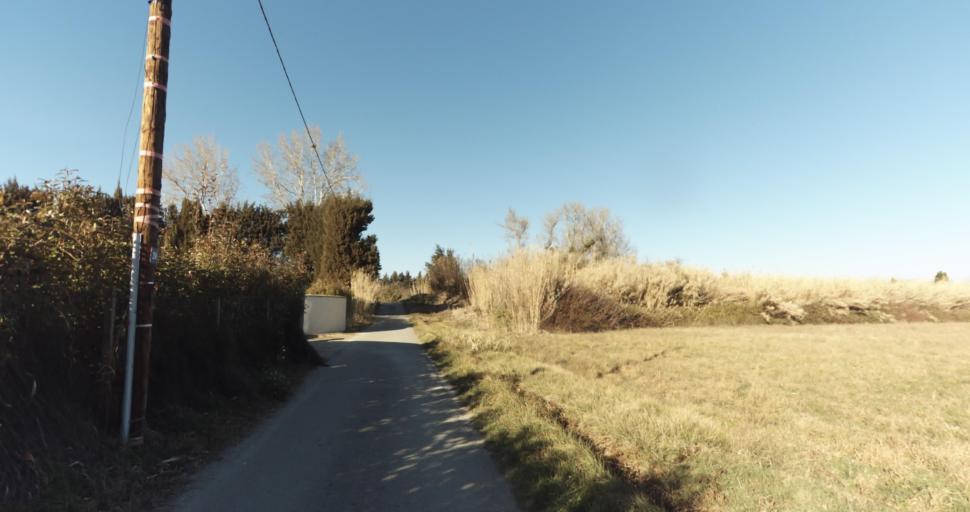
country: FR
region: Provence-Alpes-Cote d'Azur
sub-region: Departement des Bouches-du-Rhone
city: Barbentane
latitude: 43.9138
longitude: 4.7708
